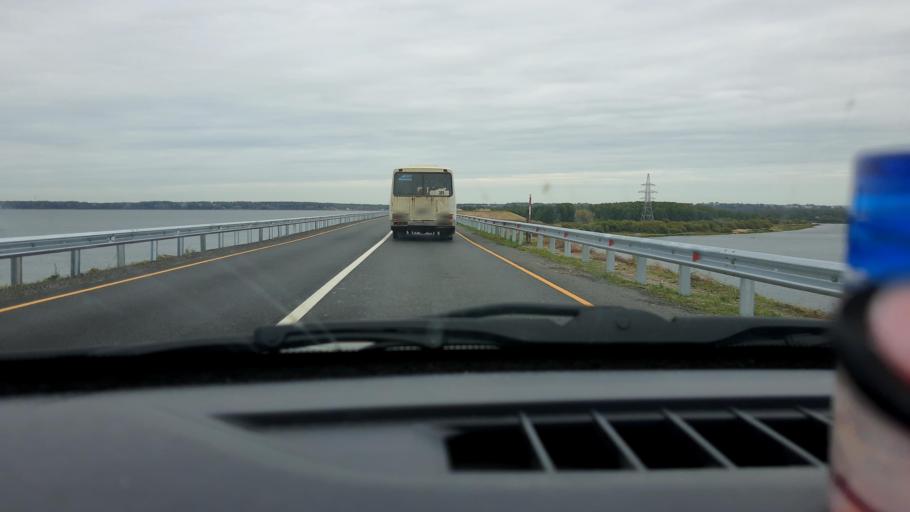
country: RU
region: Nizjnij Novgorod
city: Zavolzh'ye
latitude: 56.6602
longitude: 43.3808
